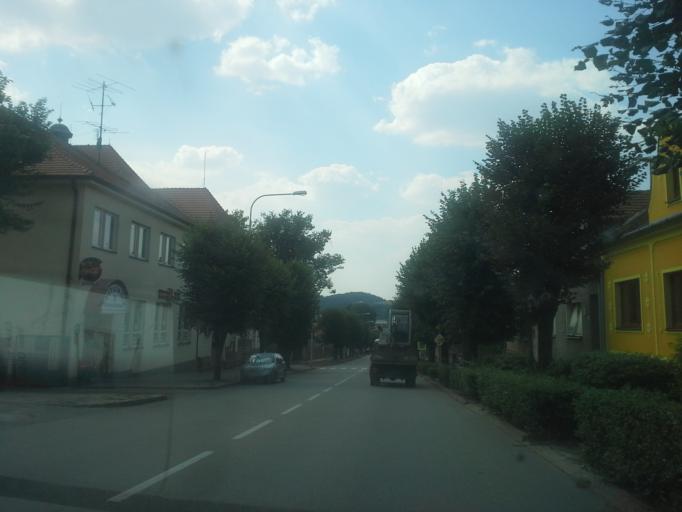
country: CZ
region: South Moravian
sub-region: Okres Blansko
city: Boskovice
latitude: 49.4913
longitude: 16.6594
